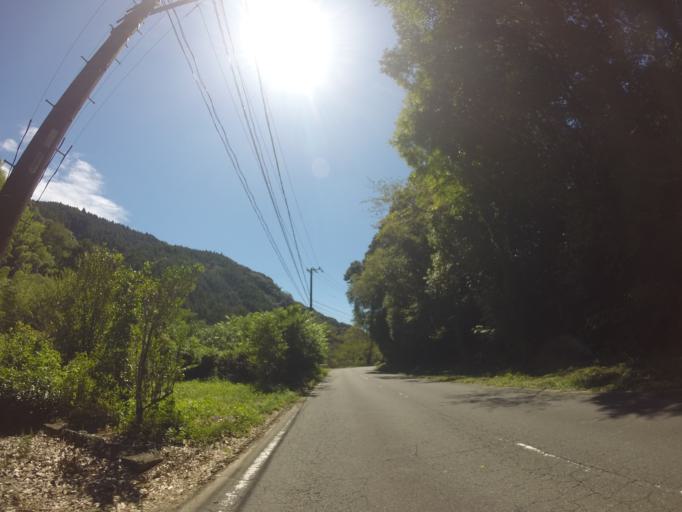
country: JP
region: Shizuoka
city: Fujieda
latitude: 34.9628
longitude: 138.2118
